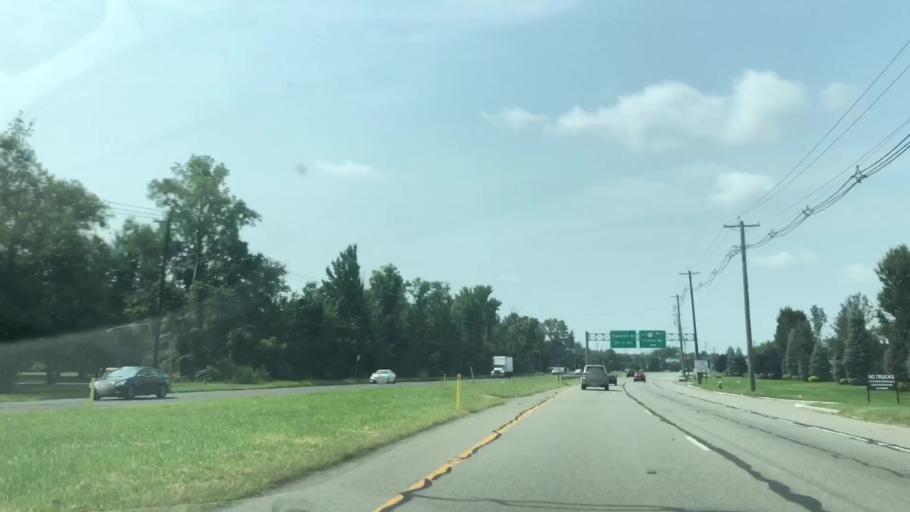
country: US
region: New Jersey
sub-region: Essex County
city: Fairfield
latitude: 40.8724
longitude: -74.3045
